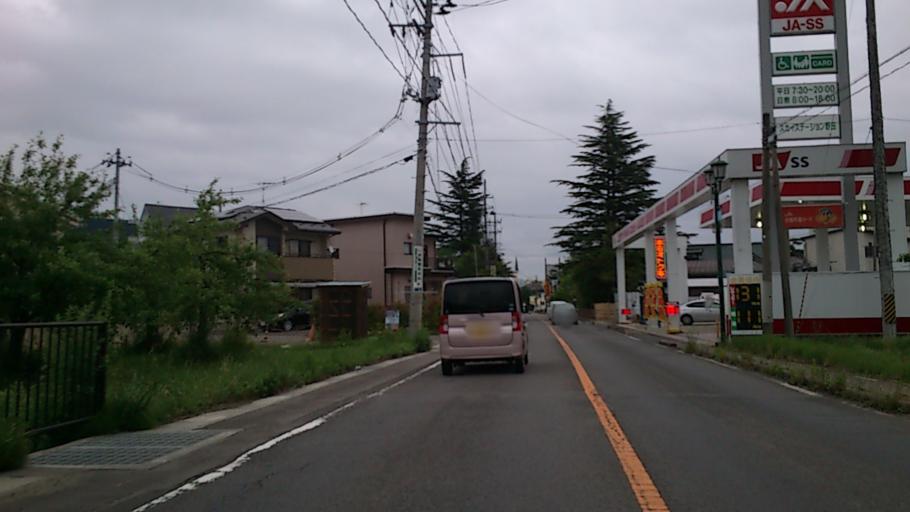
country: JP
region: Fukushima
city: Fukushima-shi
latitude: 37.7581
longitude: 140.4233
